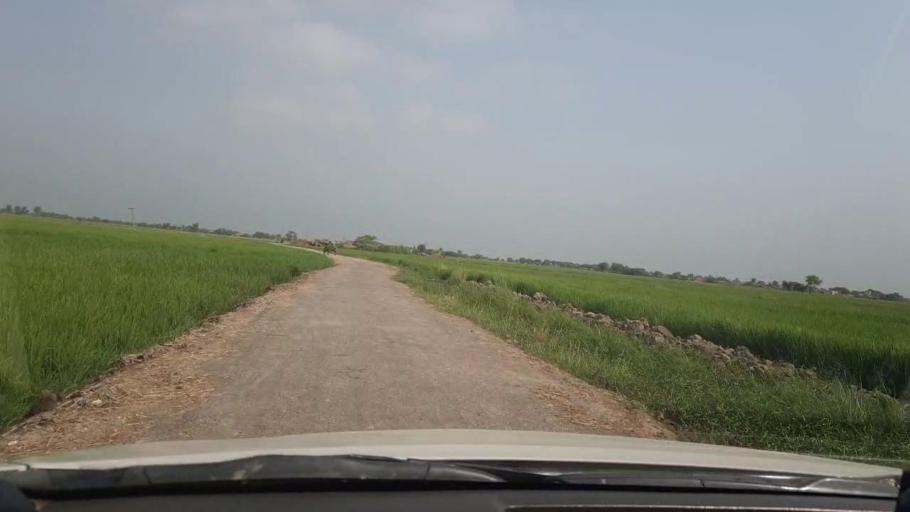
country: PK
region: Sindh
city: Shikarpur
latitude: 27.9874
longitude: 68.6089
